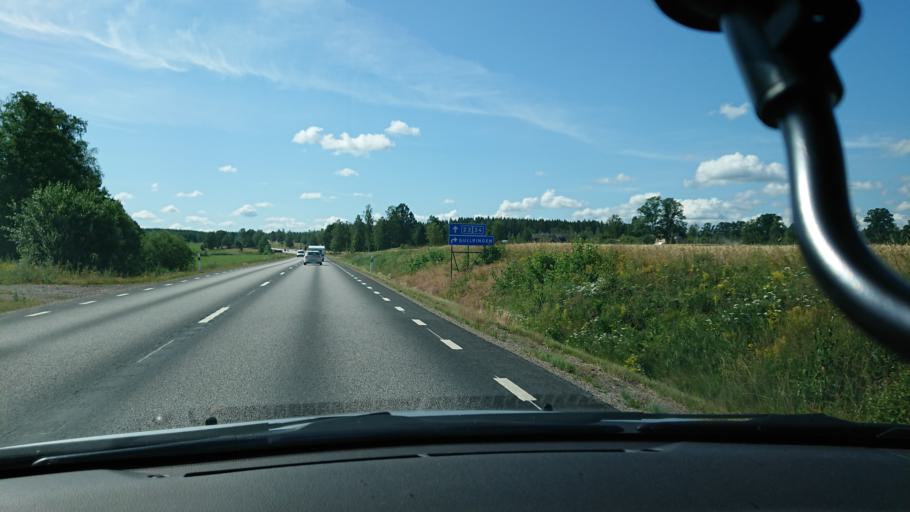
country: SE
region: Kalmar
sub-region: Vimmerby Kommun
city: Sodra Vi
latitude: 57.8052
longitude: 15.7543
